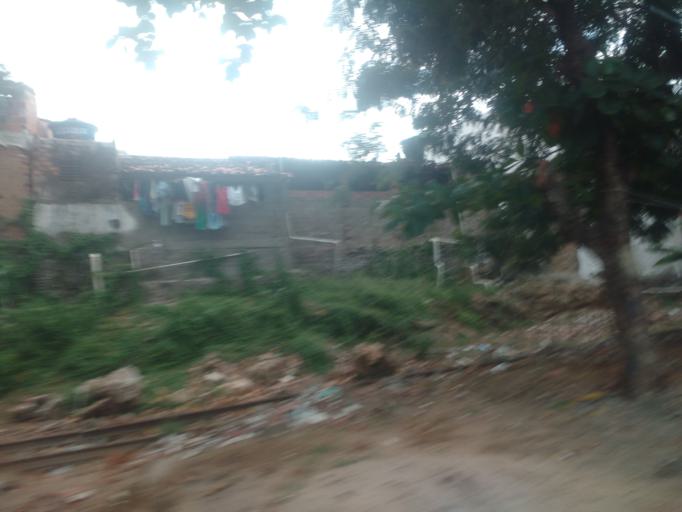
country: BR
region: Alagoas
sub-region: Uniao Dos Palmares
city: Uniao dos Palmares
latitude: -9.1625
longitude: -36.0299
